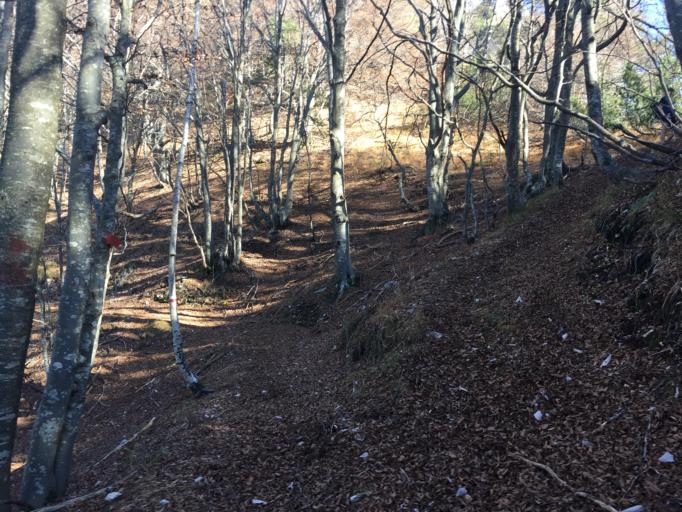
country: IT
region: Friuli Venezia Giulia
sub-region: Provincia di Udine
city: Chiusaforte
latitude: 46.4187
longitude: 13.2843
